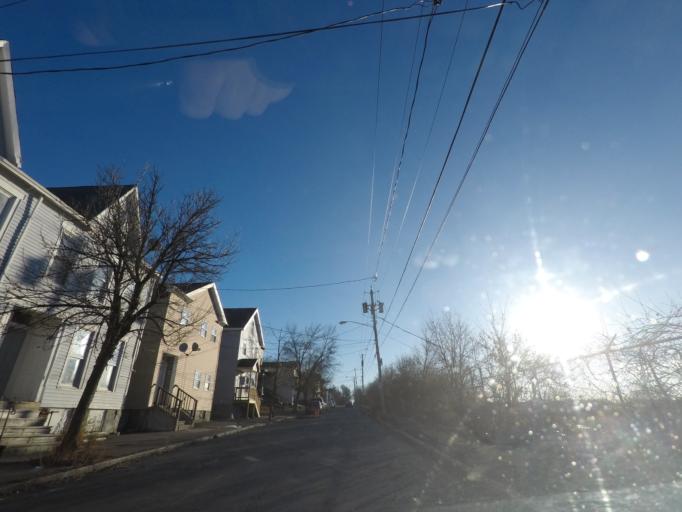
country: US
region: New York
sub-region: Albany County
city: Green Island
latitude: 42.7438
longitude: -73.6805
